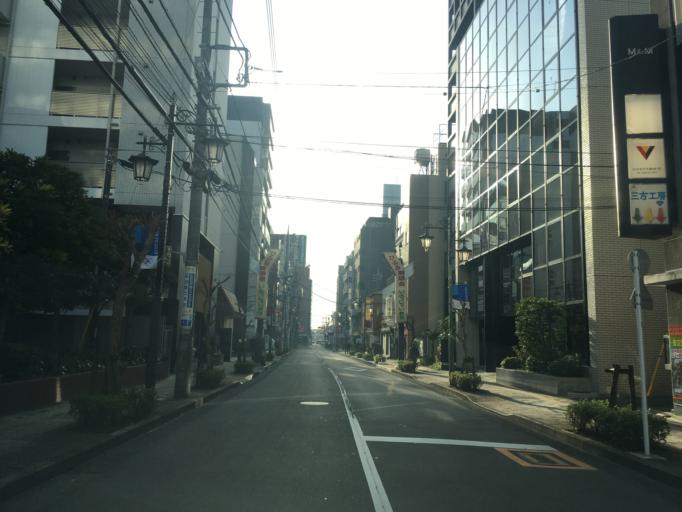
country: JP
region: Tokyo
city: Hino
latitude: 35.6955
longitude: 139.4172
